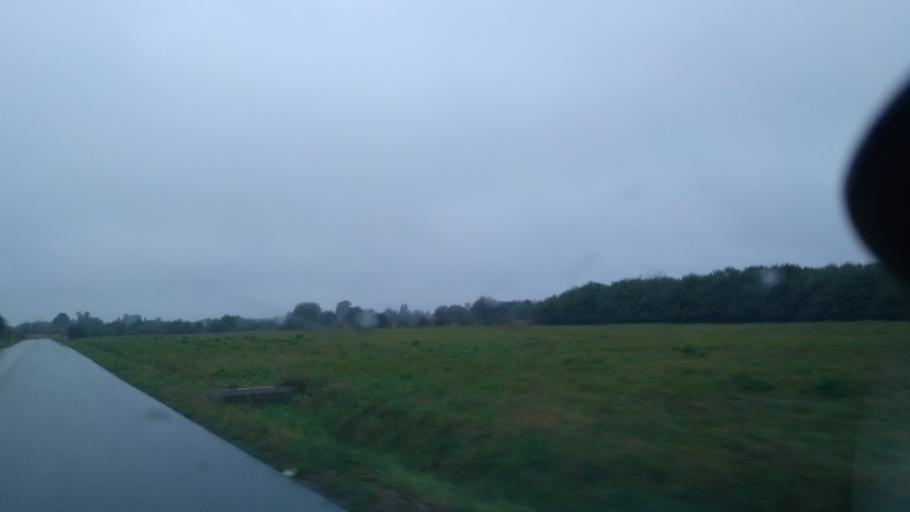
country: PL
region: Subcarpathian Voivodeship
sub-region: Powiat krosnienski
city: Kroscienko Wyzne
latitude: 49.6660
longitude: 21.8036
